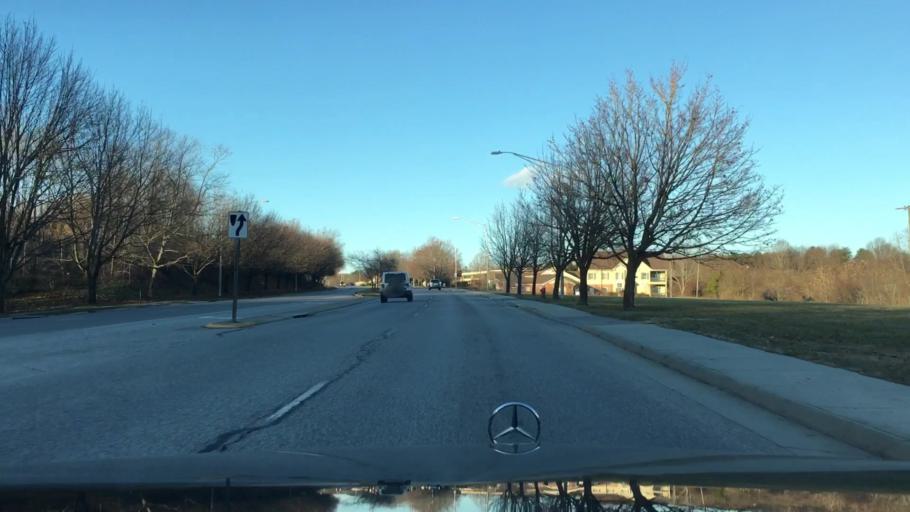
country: US
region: Virginia
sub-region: Montgomery County
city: Merrimac
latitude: 37.2035
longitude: -80.3991
